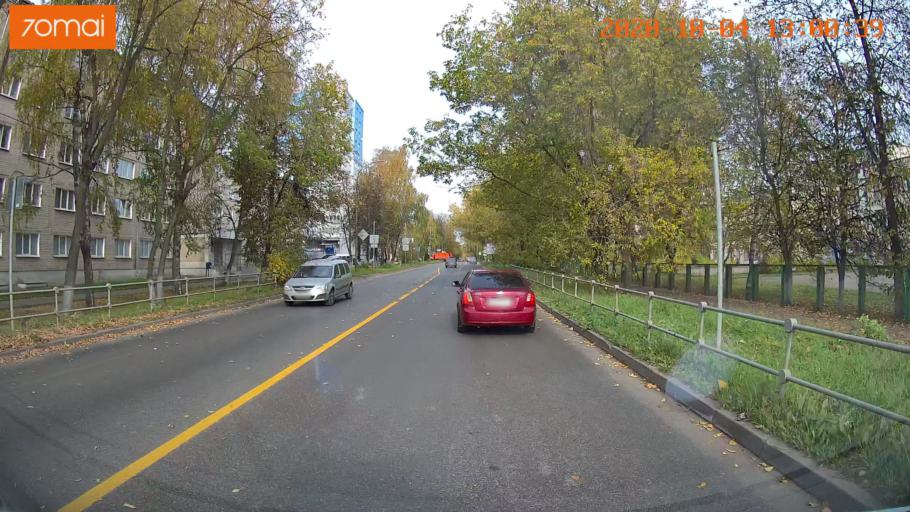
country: RU
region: Ivanovo
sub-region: Gorod Ivanovo
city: Ivanovo
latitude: 57.0212
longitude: 40.9649
